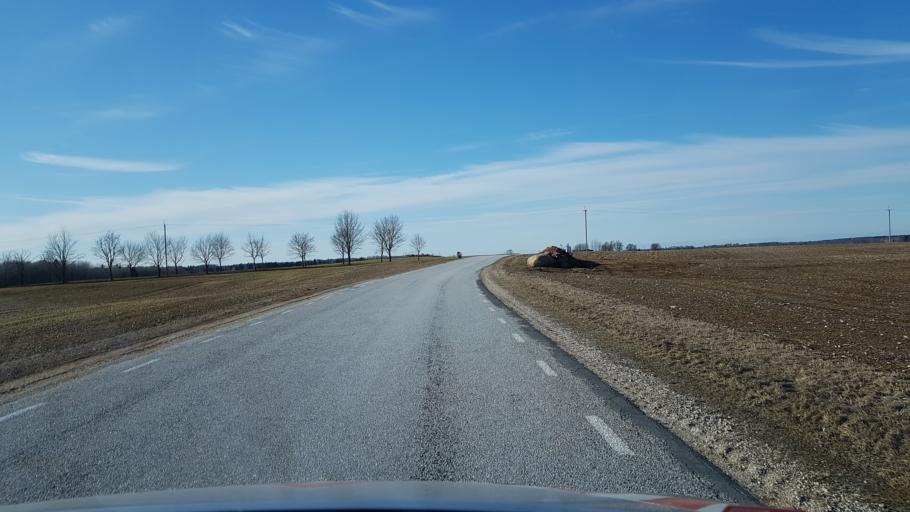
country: EE
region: Laeaene-Virumaa
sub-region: Kadrina vald
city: Kadrina
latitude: 59.2855
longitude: 26.1795
